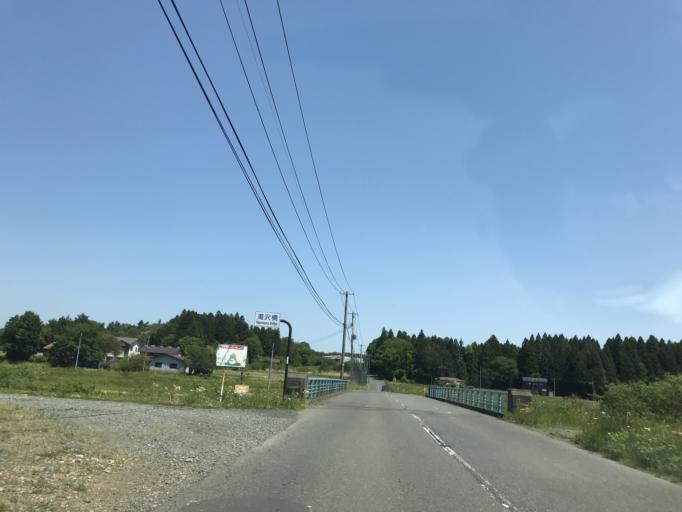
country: JP
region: Iwate
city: Kitakami
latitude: 39.2037
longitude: 141.0664
